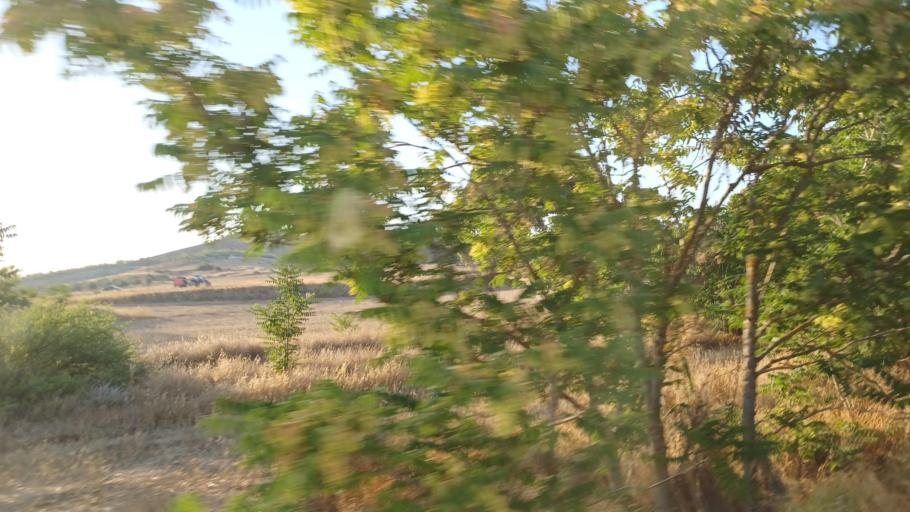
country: CY
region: Larnaka
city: Athienou
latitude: 35.0482
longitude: 33.4983
